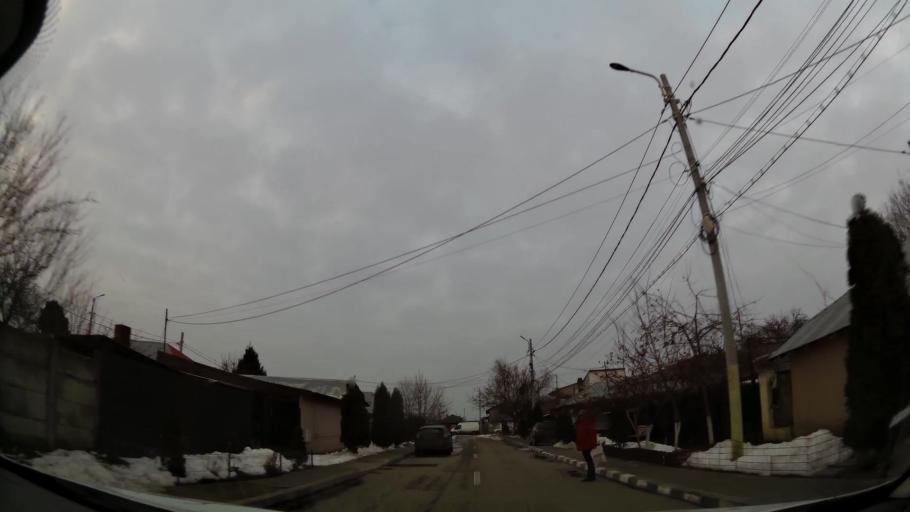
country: RO
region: Ilfov
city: Dobroesti
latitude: 44.4561
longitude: 26.1830
